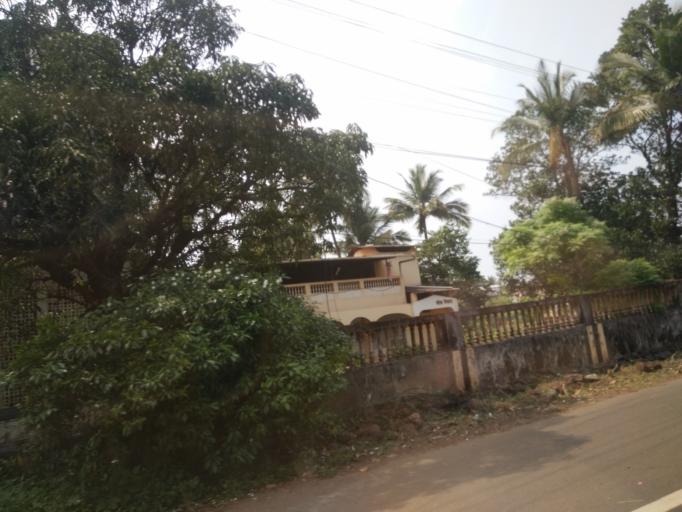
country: IN
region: Goa
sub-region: North Goa
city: Panaji
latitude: 15.5232
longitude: 73.8275
